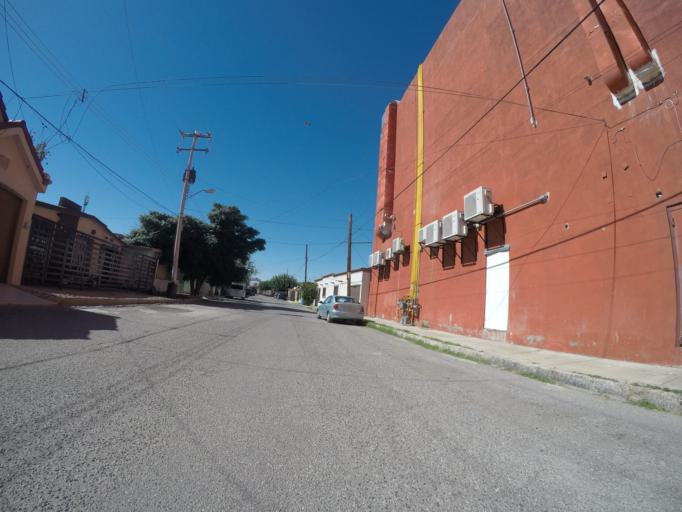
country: MX
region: Chihuahua
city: Ciudad Juarez
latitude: 31.7219
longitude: -106.4199
